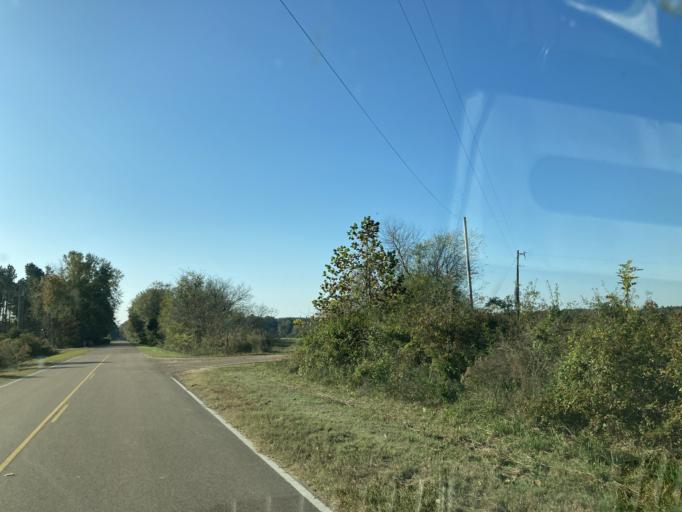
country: US
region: Mississippi
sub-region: Madison County
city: Canton
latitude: 32.7277
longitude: -90.1667
